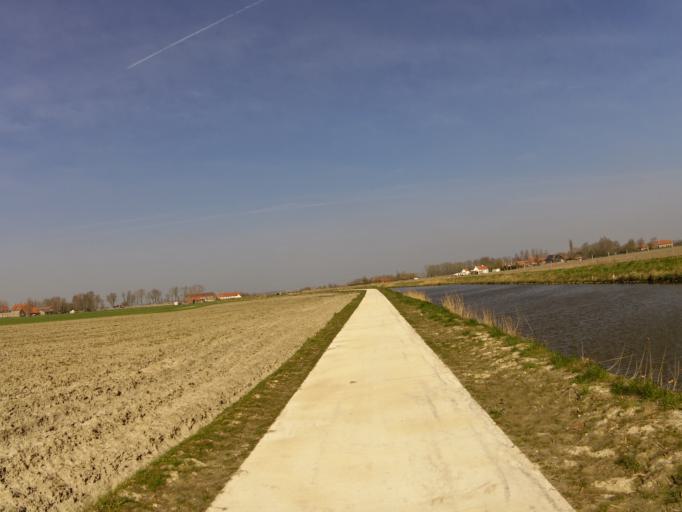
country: BE
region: Flanders
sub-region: Provincie West-Vlaanderen
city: Gistel
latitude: 51.1766
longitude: 2.9570
